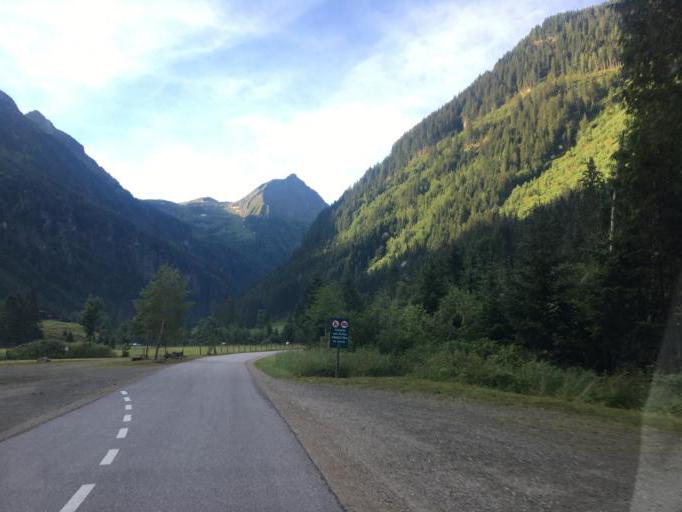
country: AT
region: Styria
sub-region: Politischer Bezirk Liezen
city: Haus
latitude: 47.3301
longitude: 13.7545
